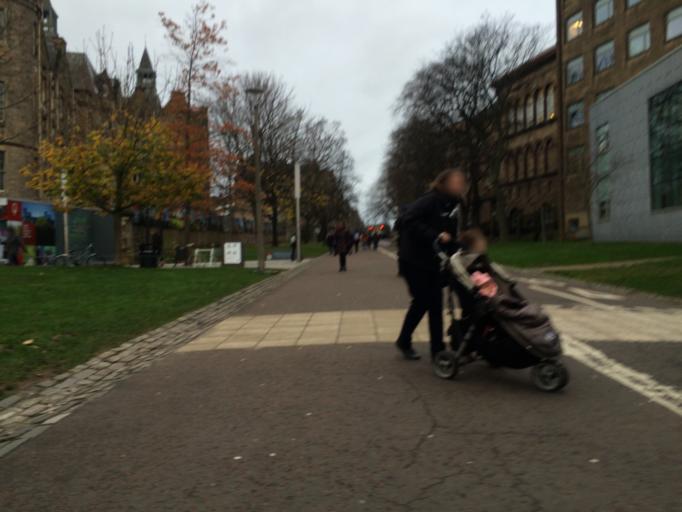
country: GB
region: Scotland
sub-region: Edinburgh
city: Edinburgh
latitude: 55.9440
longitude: -3.1914
